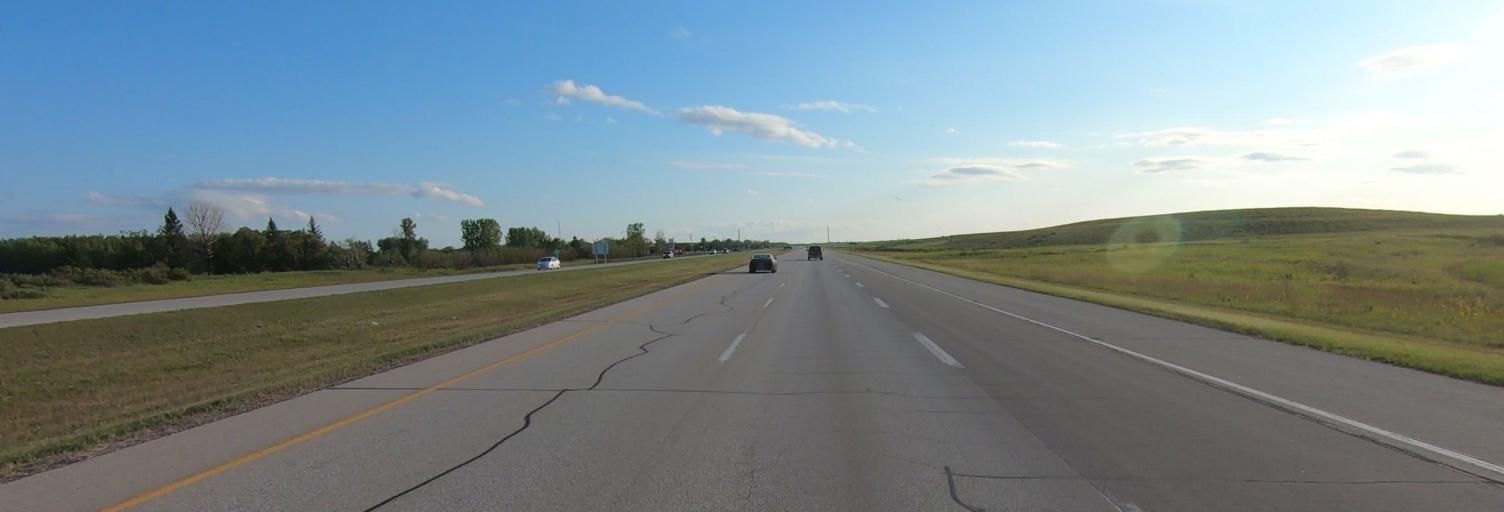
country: CA
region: Manitoba
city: Selkirk
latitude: 50.0133
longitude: -96.9502
